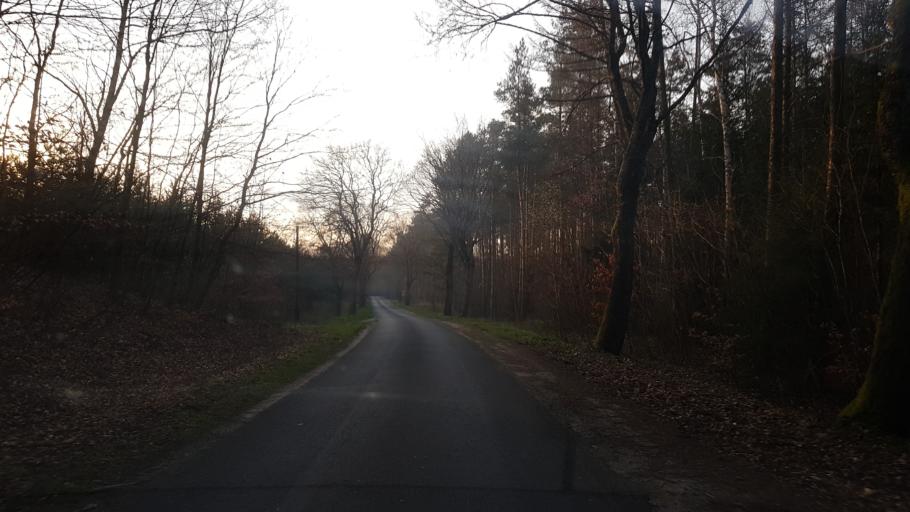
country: PL
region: West Pomeranian Voivodeship
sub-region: Powiat swidwinski
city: Swidwin
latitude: 53.7345
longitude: 15.7238
